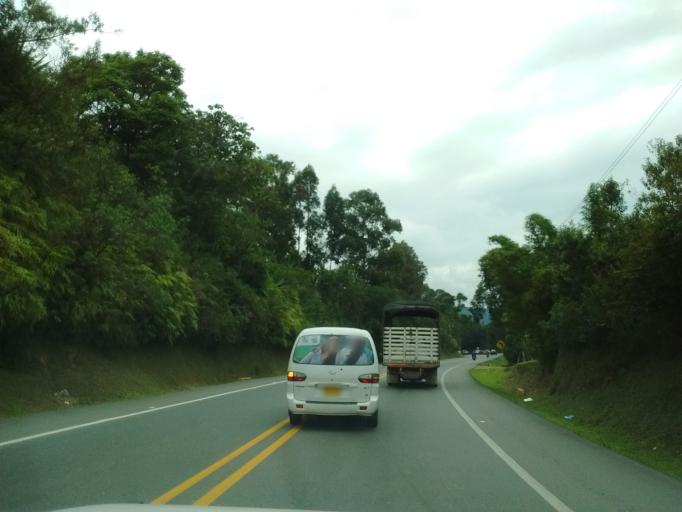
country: CO
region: Cauca
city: Cajibio
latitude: 2.6114
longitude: -76.5205
